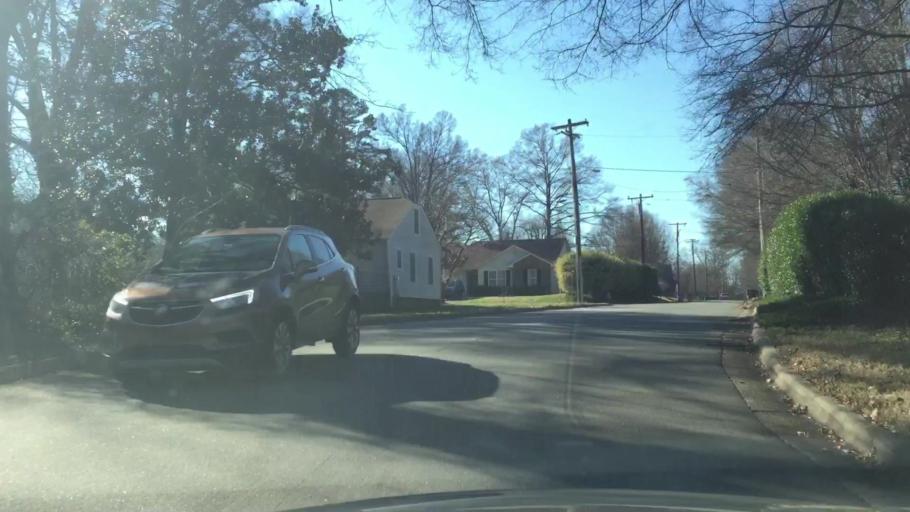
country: US
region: North Carolina
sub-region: Iredell County
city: Mooresville
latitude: 35.5852
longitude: -80.7948
